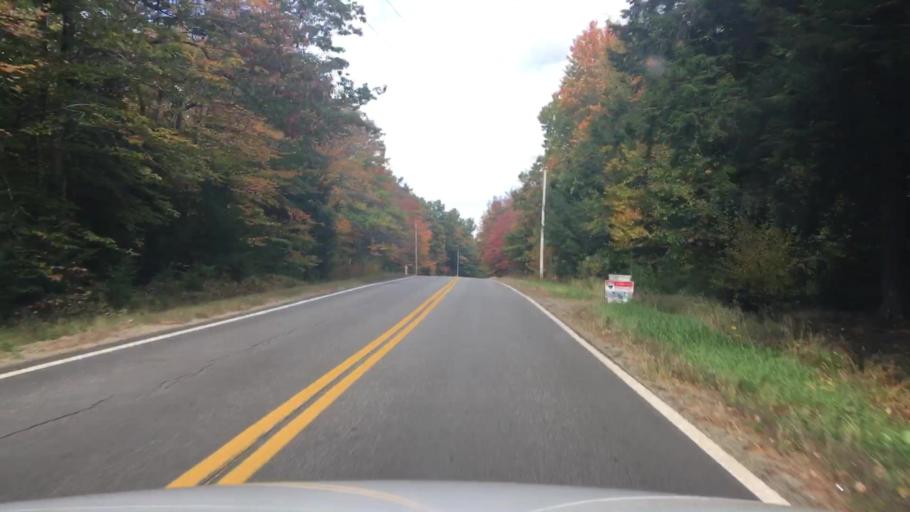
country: US
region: Maine
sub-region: Knox County
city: Hope
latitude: 44.3282
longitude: -69.1353
